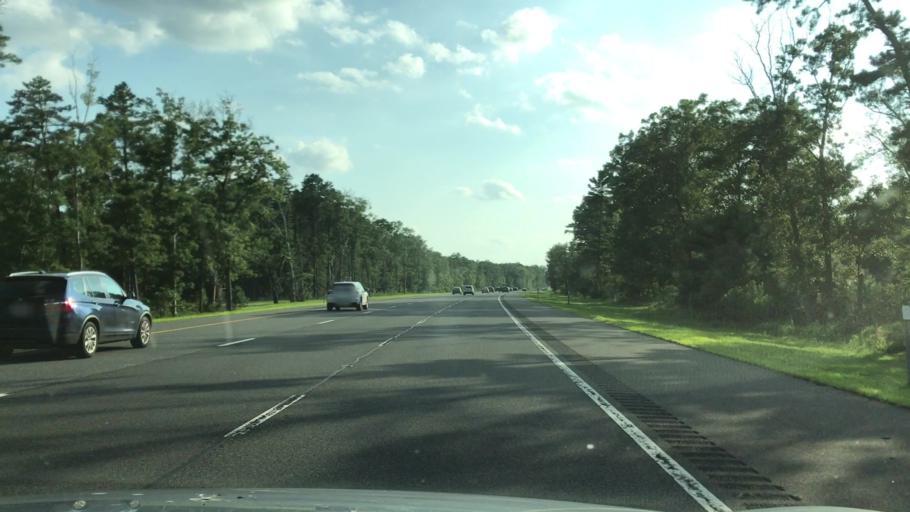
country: US
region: New Jersey
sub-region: Ocean County
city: Tuckerton
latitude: 39.6289
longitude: -74.3898
